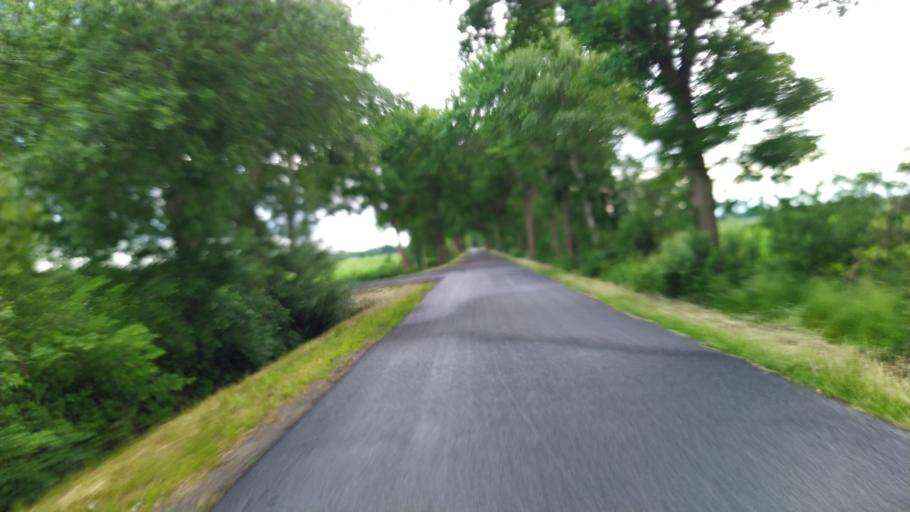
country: DE
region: Lower Saxony
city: Sandbostel
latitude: 53.4235
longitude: 9.1655
